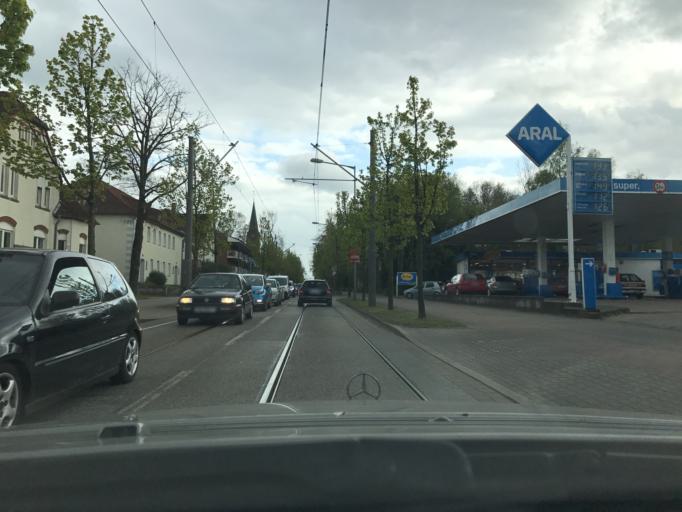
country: DE
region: North Rhine-Westphalia
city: Waltrop
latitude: 51.5934
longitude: 7.4402
